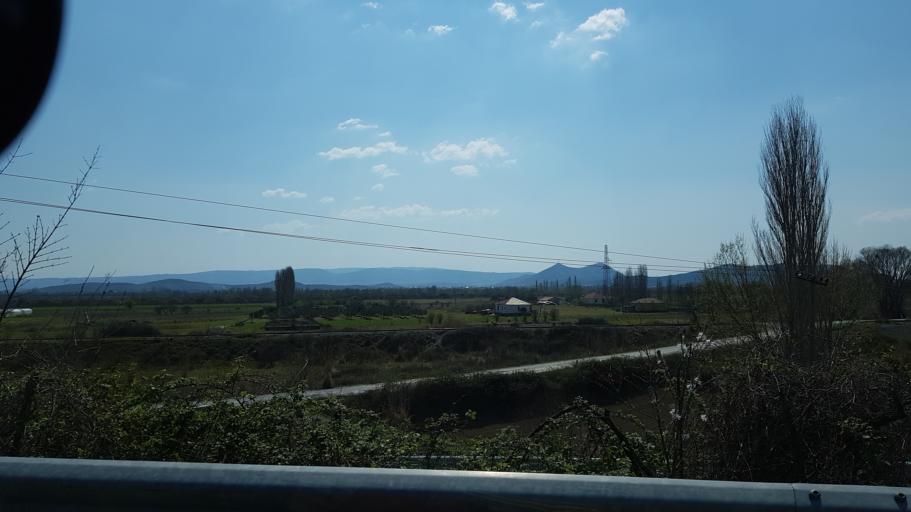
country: AL
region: Shkoder
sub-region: Rrethi i Shkodres
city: Guri i Zi
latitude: 42.0139
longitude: 19.5791
